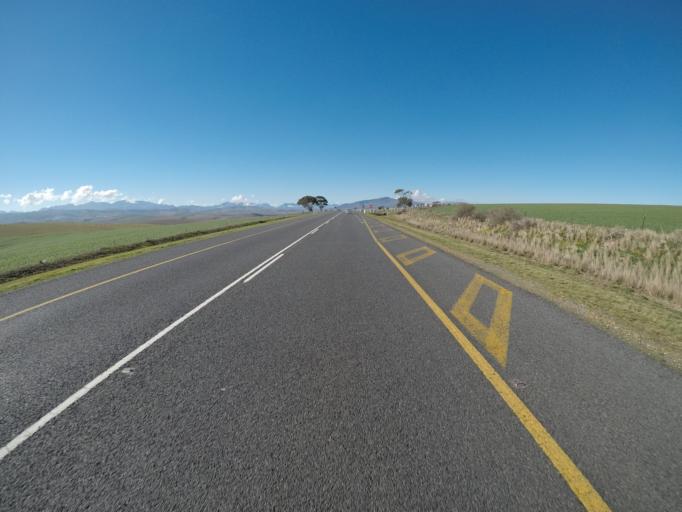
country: ZA
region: Western Cape
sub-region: Overberg District Municipality
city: Caledon
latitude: -34.2228
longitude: 19.3030
